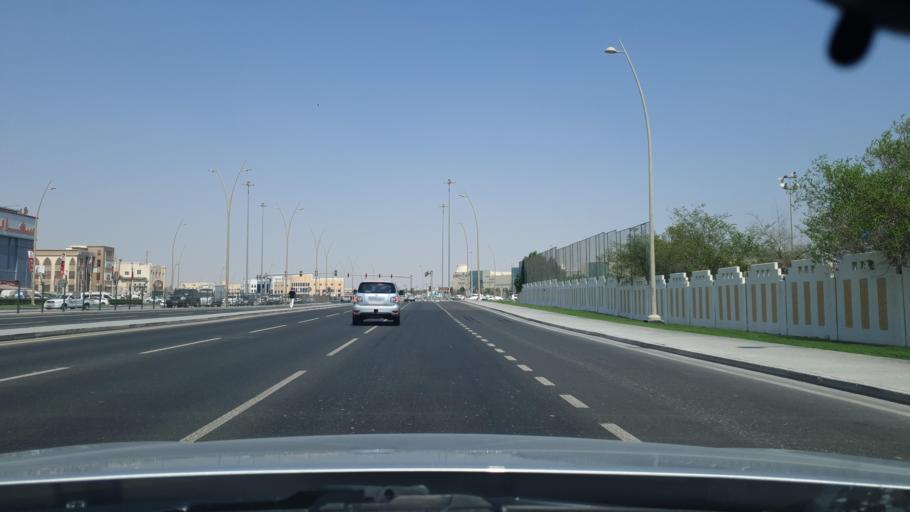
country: QA
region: Al Khawr
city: Al Khawr
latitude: 25.6720
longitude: 51.5011
